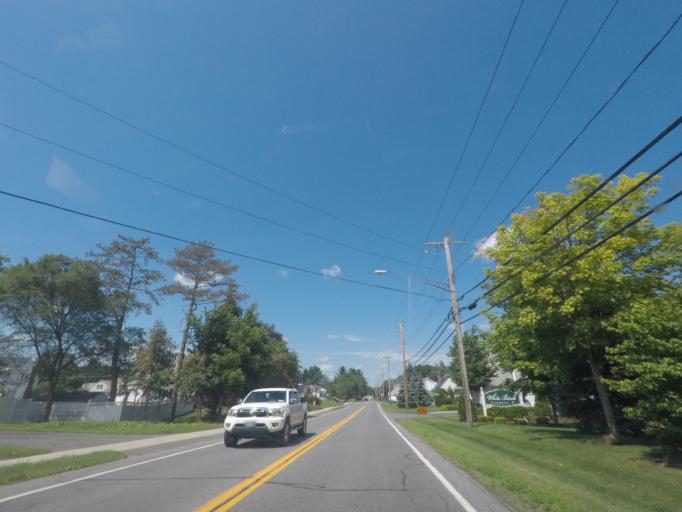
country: US
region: New York
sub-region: Schenectady County
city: Rotterdam
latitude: 42.7757
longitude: -73.9587
